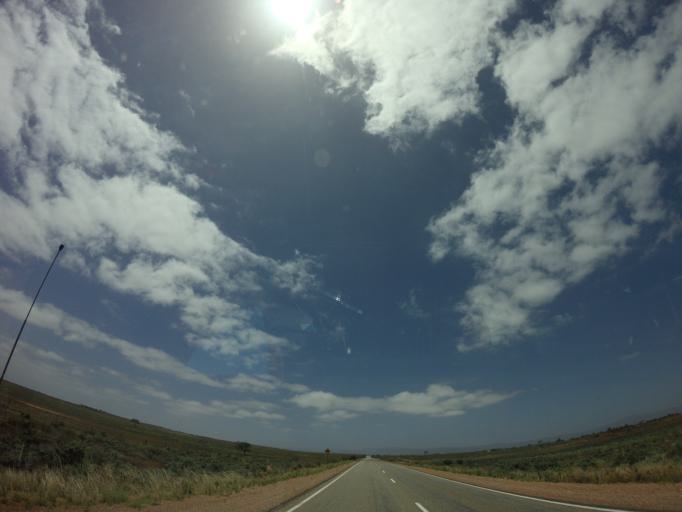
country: AU
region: South Australia
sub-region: Port Augusta
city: Port Augusta West
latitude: -32.4903
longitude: 137.7164
